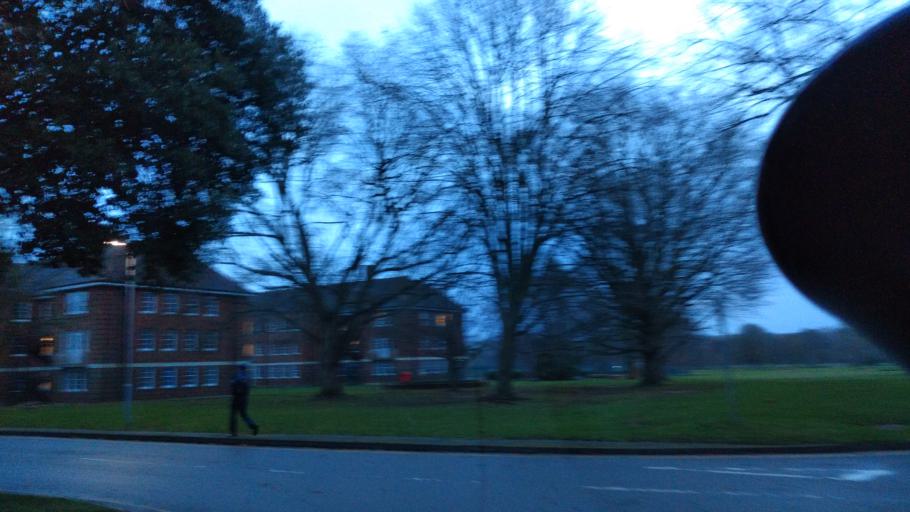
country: GB
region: England
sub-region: Oxfordshire
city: Shrivenham
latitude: 51.6023
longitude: -1.6438
